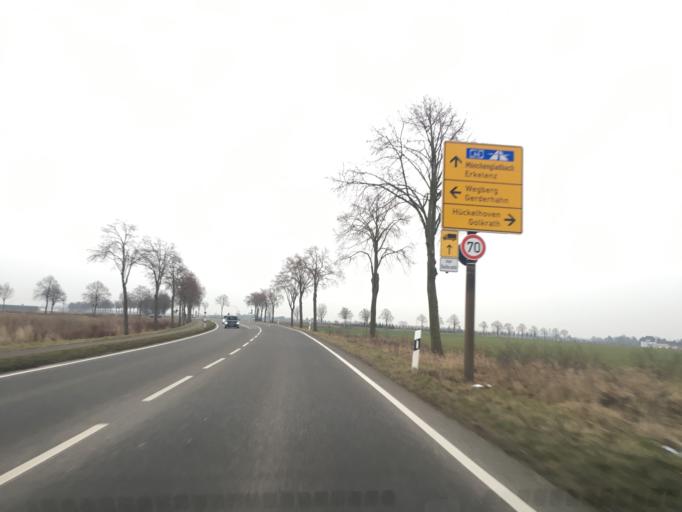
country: DE
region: North Rhine-Westphalia
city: Huckelhoven
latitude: 51.0930
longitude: 6.2398
